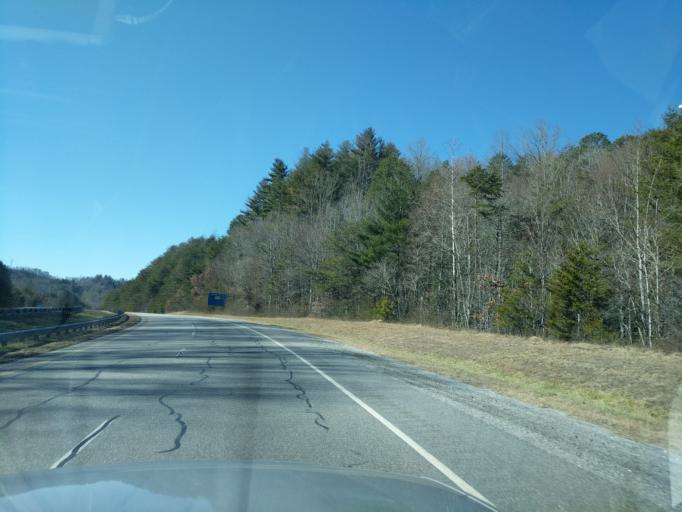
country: US
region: North Carolina
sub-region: Swain County
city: Bryson City
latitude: 35.4262
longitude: -83.4133
